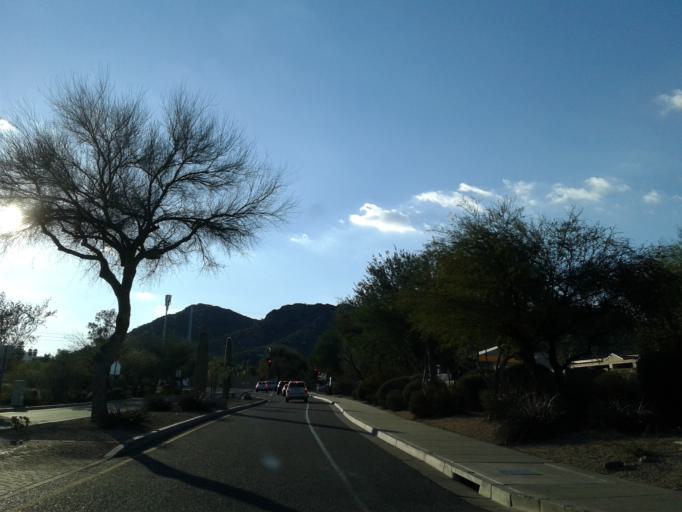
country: US
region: Arizona
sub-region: Maricopa County
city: Paradise Valley
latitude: 33.5683
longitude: -111.9762
